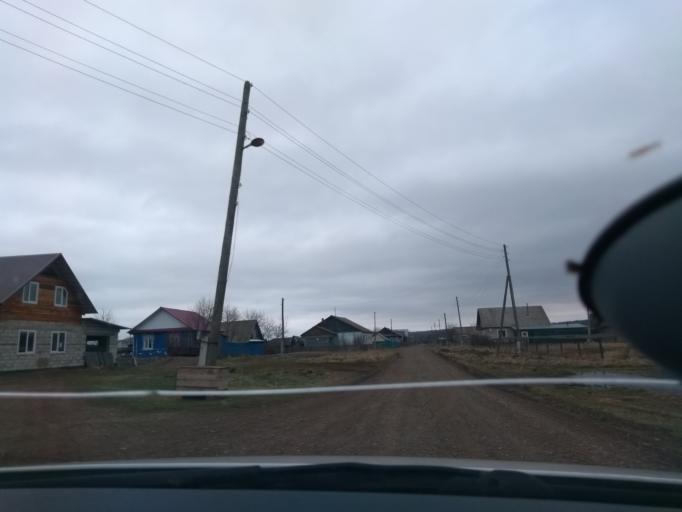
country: RU
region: Perm
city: Orda
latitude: 57.2214
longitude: 56.5952
